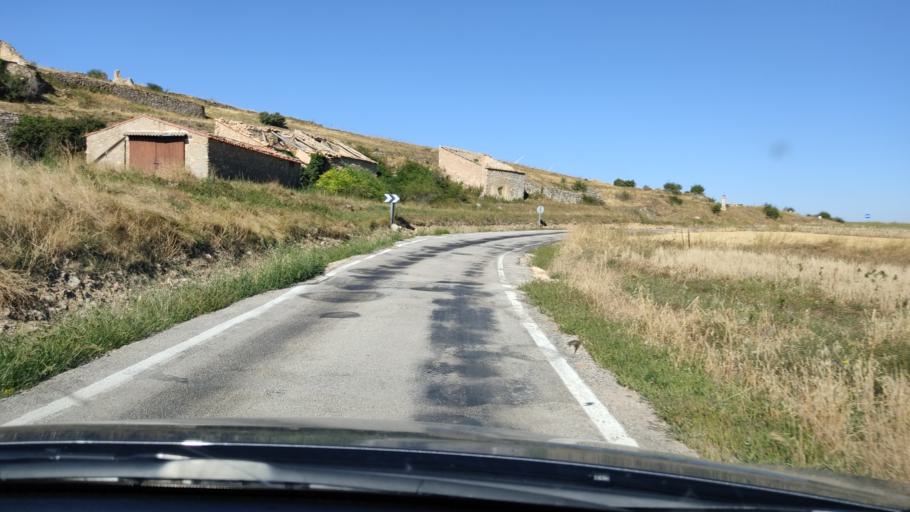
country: ES
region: Aragon
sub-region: Provincia de Teruel
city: Allueva
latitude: 40.9999
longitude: -1.0144
